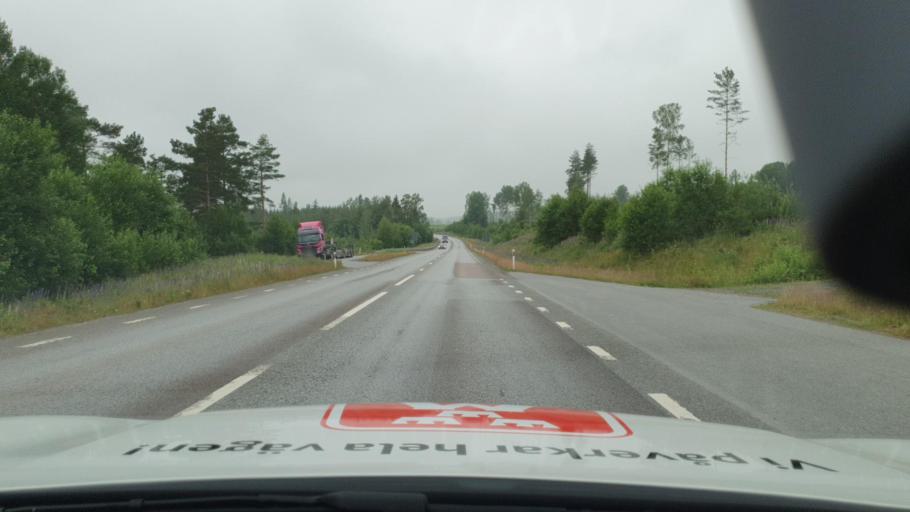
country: SE
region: Vaermland
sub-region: Karlstads Kommun
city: Edsvalla
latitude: 59.5595
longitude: 13.1872
